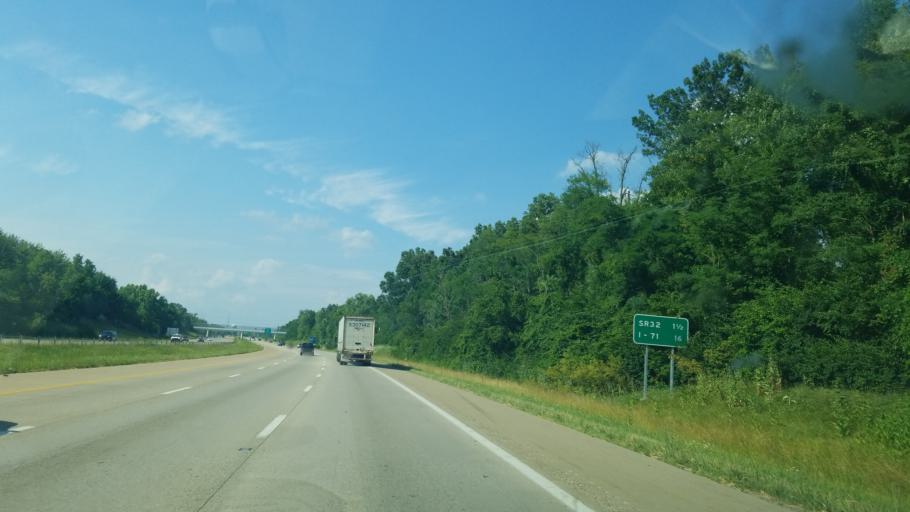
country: US
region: Ohio
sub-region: Clermont County
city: Withamsville
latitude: 39.0797
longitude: -84.2906
